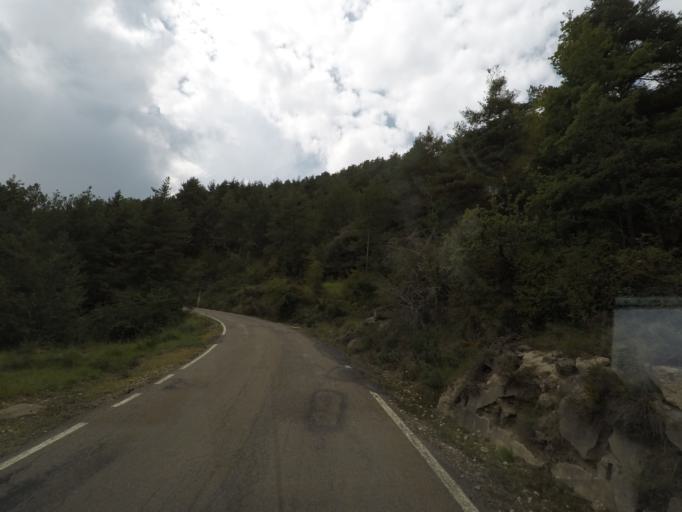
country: ES
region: Aragon
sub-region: Provincia de Huesca
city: Boltana
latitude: 42.4058
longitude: -0.0287
